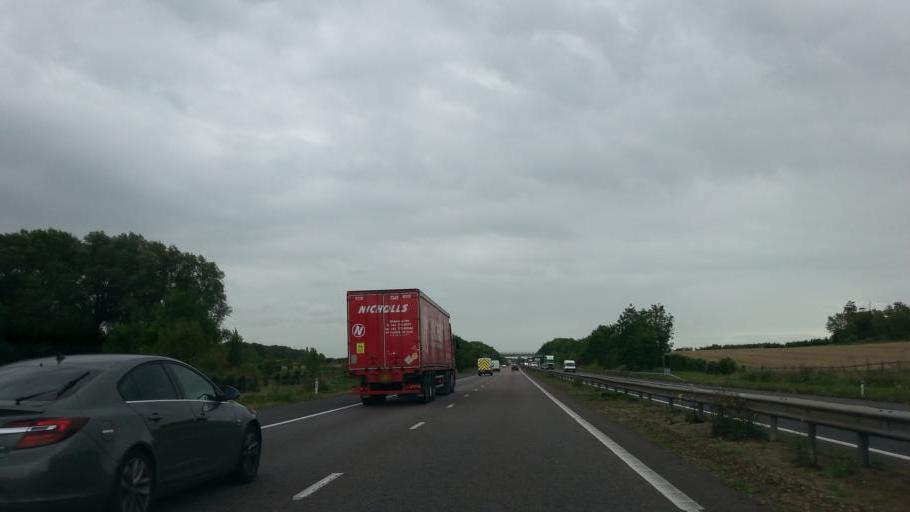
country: GB
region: England
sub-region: Cambridgeshire
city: Harston
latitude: 52.1324
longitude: 0.1157
